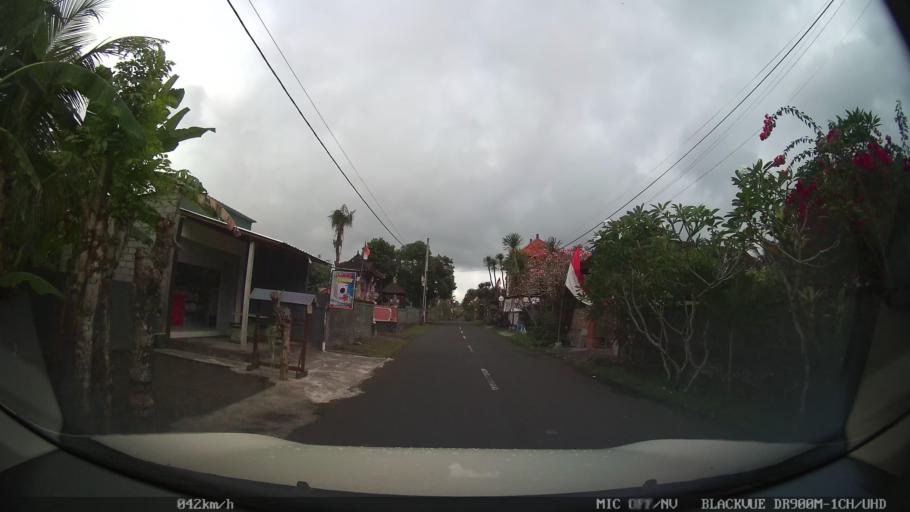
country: ID
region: Bali
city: Banjar Cemenggon
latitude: -8.5369
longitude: 115.1915
